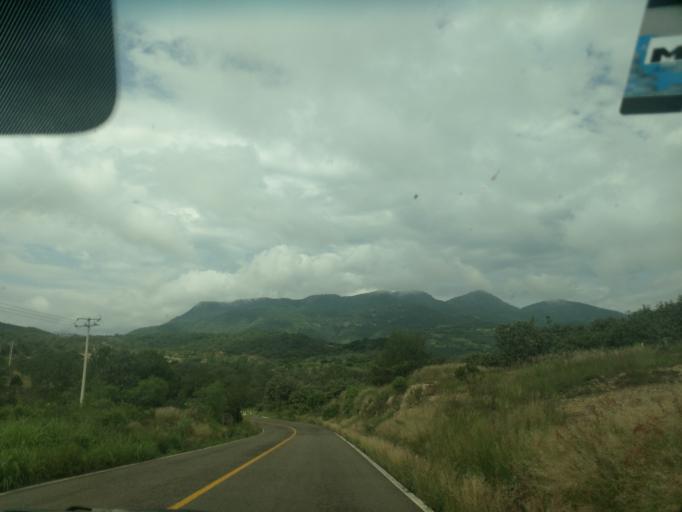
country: MX
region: Jalisco
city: El Salto
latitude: 20.3833
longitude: -104.5399
